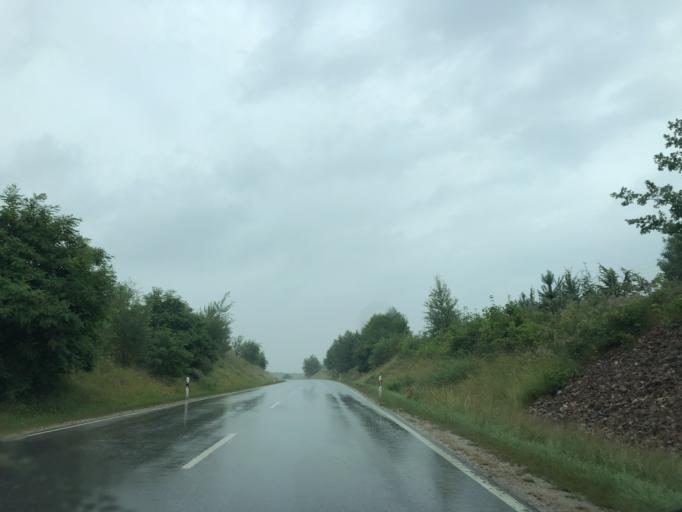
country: DE
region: Bavaria
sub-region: Upper Bavaria
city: Au in der Hallertau
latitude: 48.5454
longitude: 11.7406
